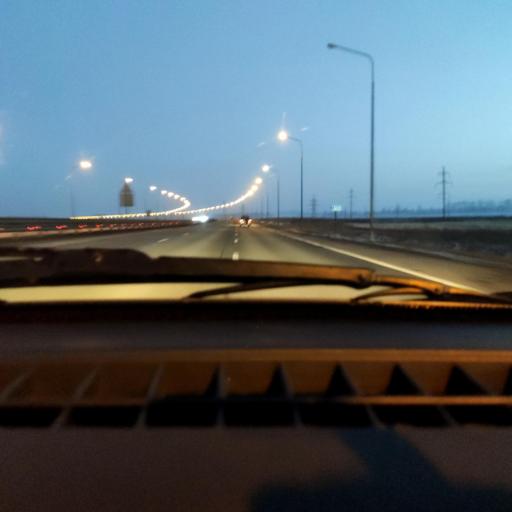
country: RU
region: Bashkortostan
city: Asanovo
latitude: 54.8971
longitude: 55.6367
